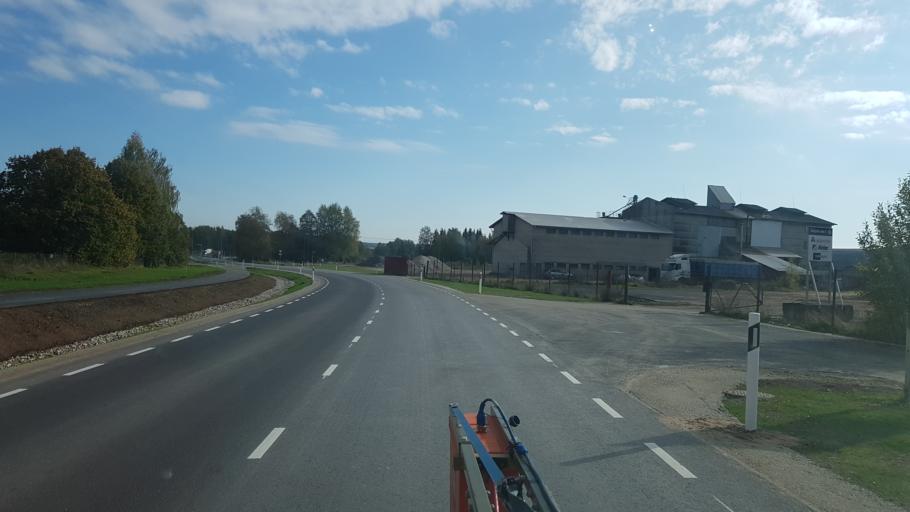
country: EE
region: Tartu
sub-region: UElenurme vald
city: Ulenurme
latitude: 58.2936
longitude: 26.7131
